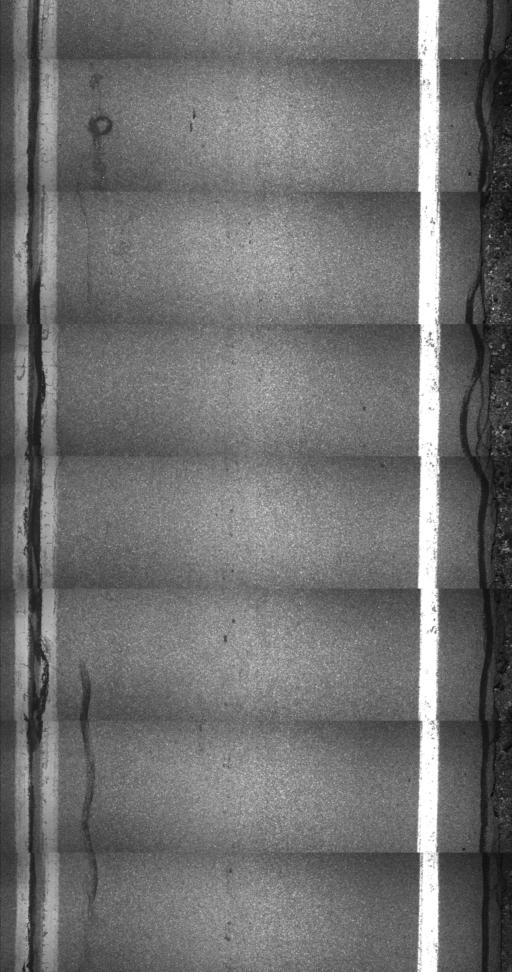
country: US
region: Vermont
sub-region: Rutland County
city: Brandon
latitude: 43.7319
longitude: -73.1806
